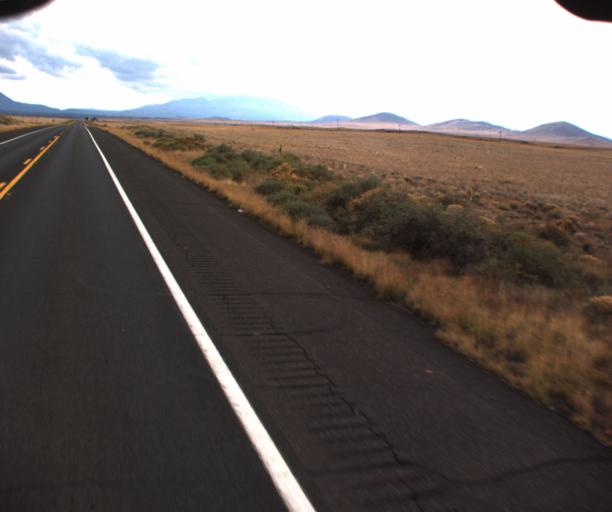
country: US
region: Arizona
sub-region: Coconino County
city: Flagstaff
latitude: 35.6113
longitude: -111.5238
